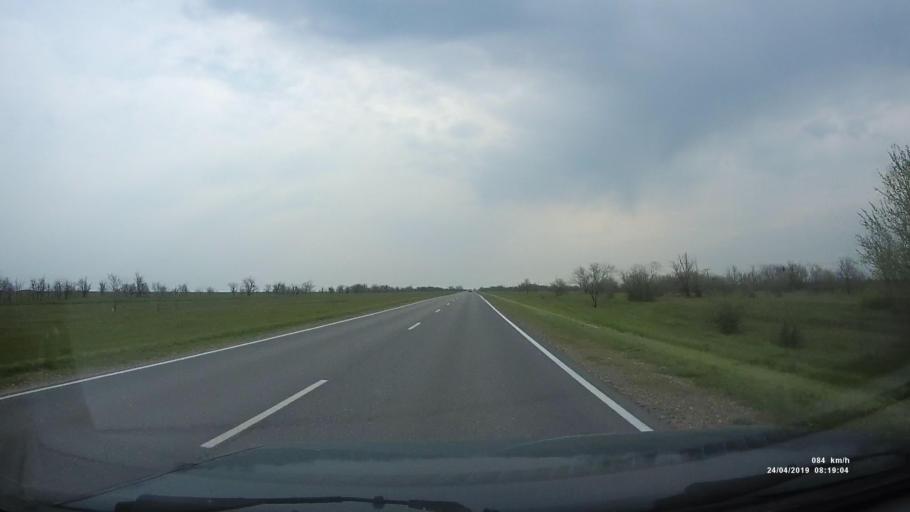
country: RU
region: Kalmykiya
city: Priyutnoye
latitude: 46.1026
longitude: 43.6590
